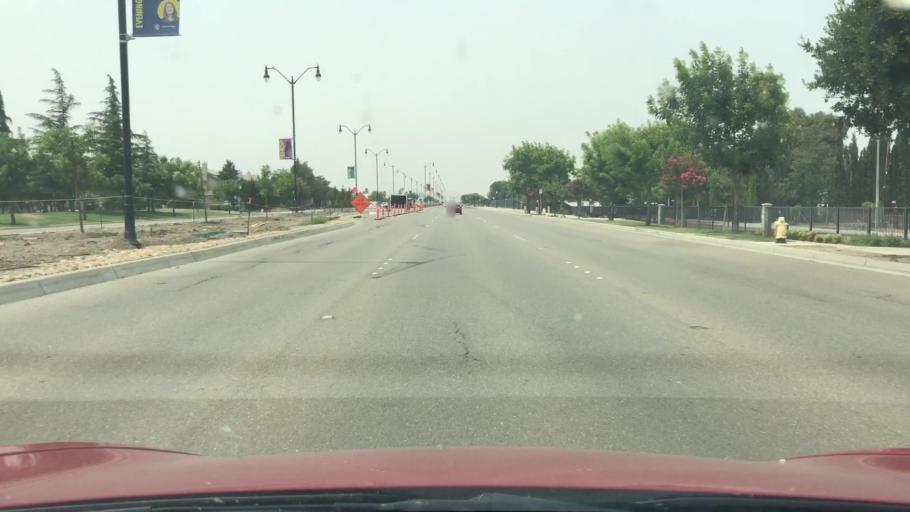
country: US
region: California
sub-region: San Joaquin County
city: Tracy
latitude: 37.7393
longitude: -121.4678
